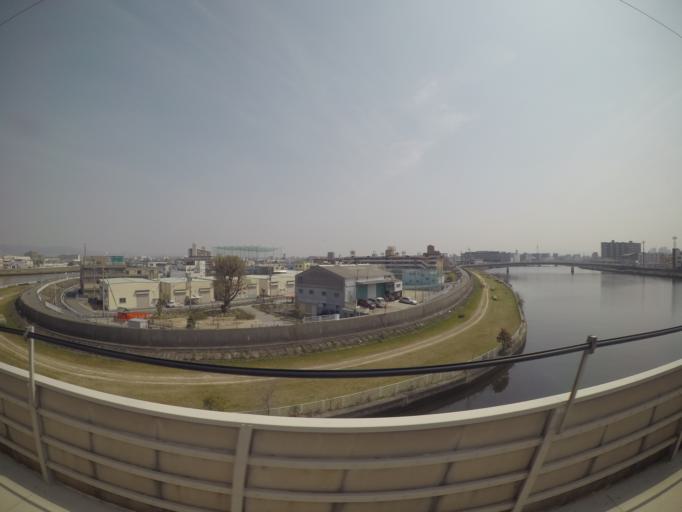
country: JP
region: Hyogo
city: Amagasaki
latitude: 34.7358
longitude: 135.4512
